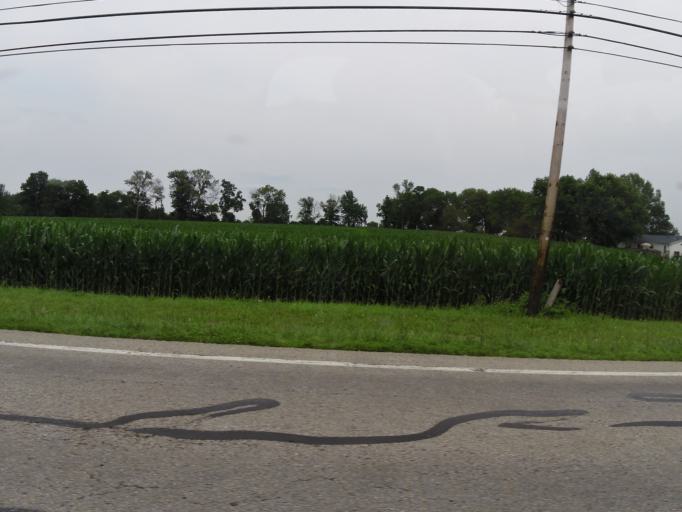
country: US
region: Ohio
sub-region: Clinton County
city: Wilmington
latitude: 39.4832
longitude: -83.9246
